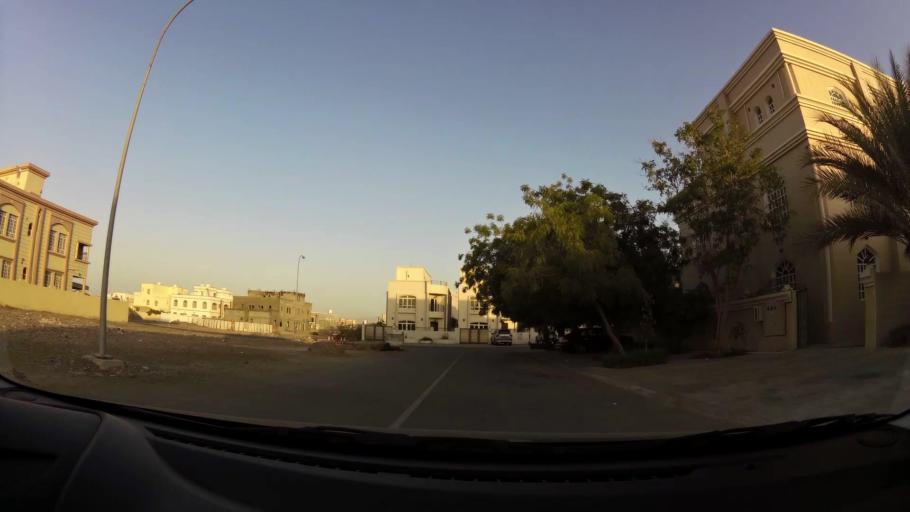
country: OM
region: Muhafazat Masqat
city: As Sib al Jadidah
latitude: 23.6118
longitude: 58.1988
